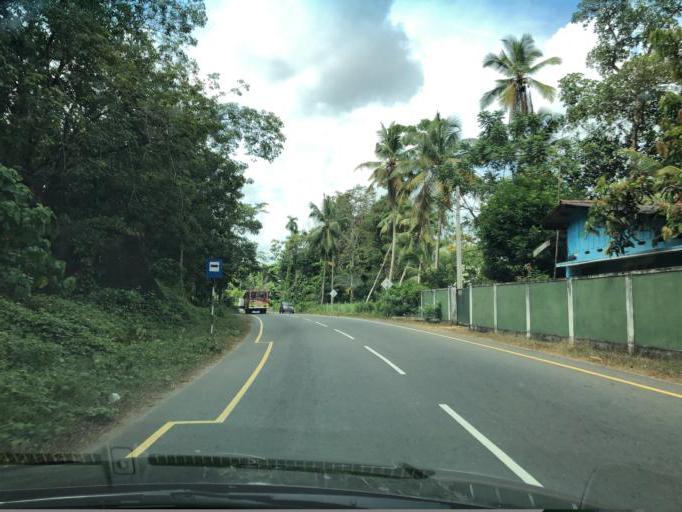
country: LK
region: Western
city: Horana South
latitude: 6.6295
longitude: 80.0783
